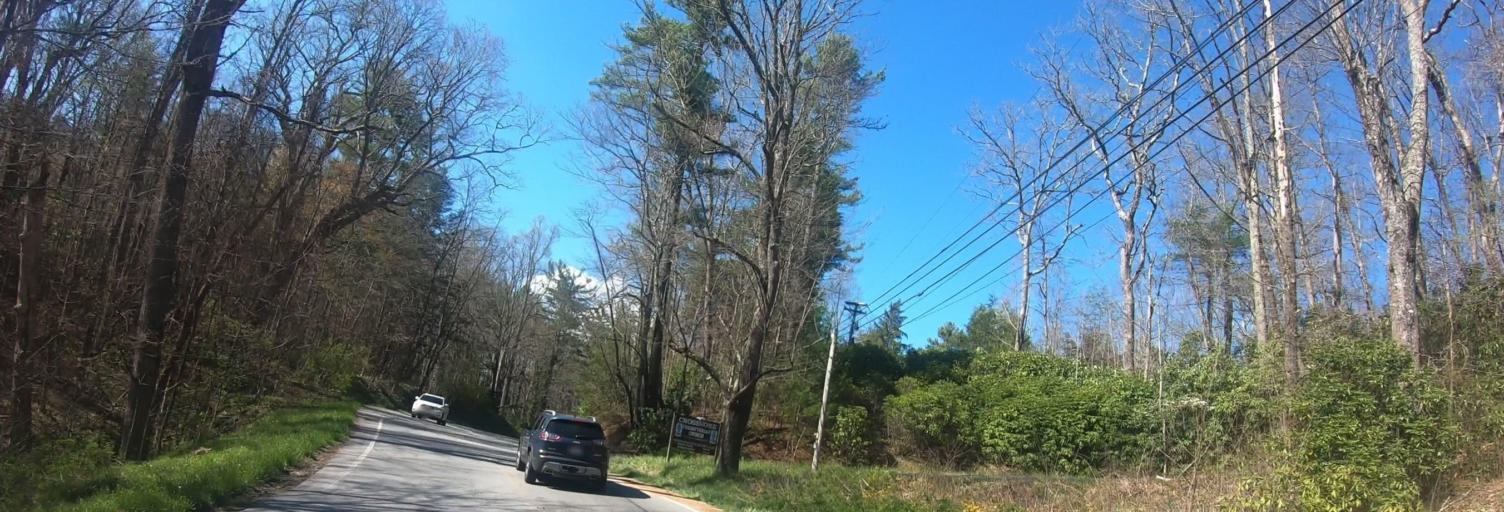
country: US
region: North Carolina
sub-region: Avery County
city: Newland
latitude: 36.0181
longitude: -81.9307
